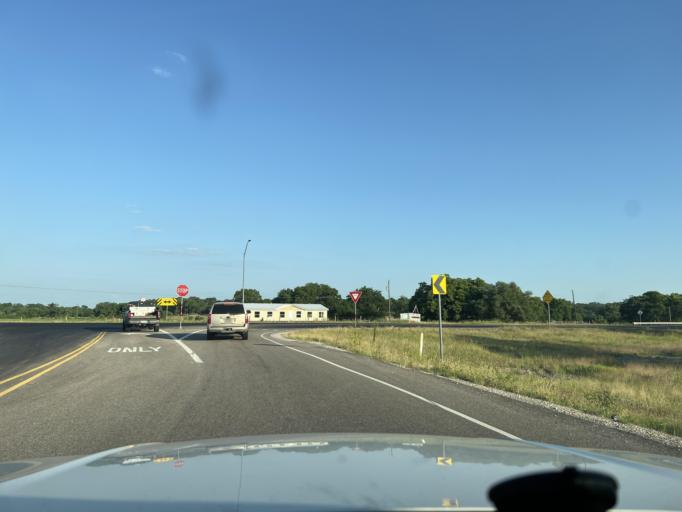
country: US
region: Texas
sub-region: Washington County
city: Brenham
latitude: 30.1979
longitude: -96.3644
